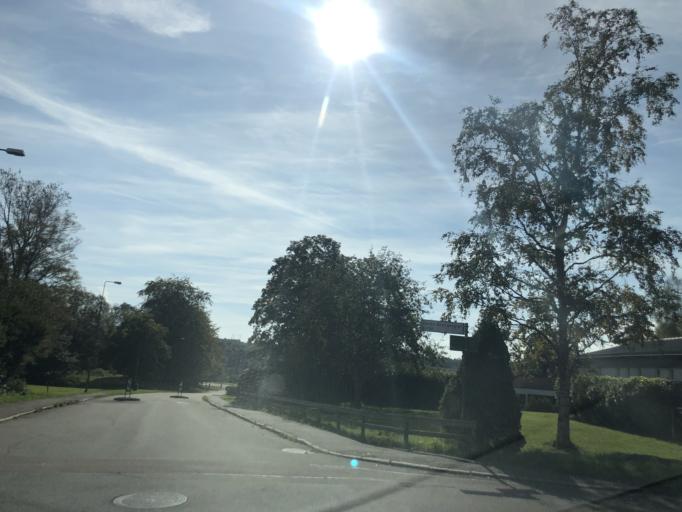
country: SE
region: Vaestra Goetaland
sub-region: Molndal
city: Moelndal
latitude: 57.6654
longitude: 12.0465
